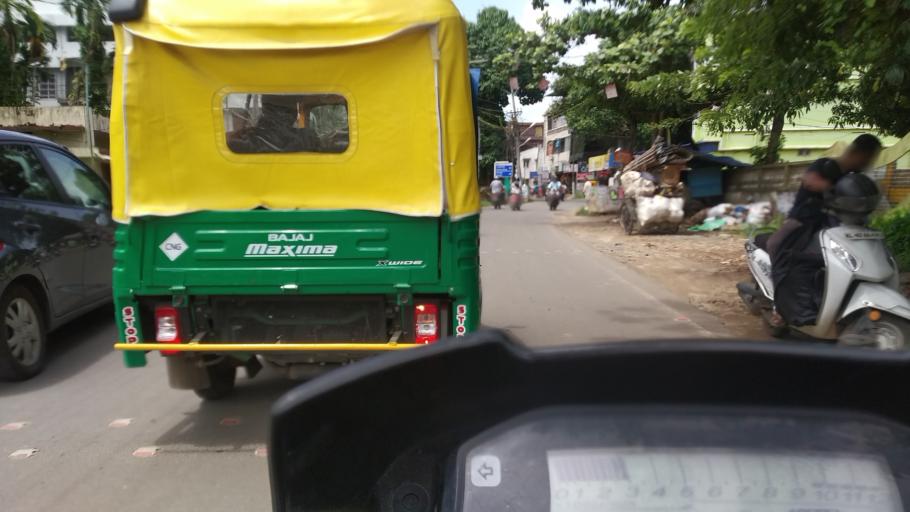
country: IN
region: Kerala
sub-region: Ernakulam
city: Cochin
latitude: 9.9860
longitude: 76.3092
